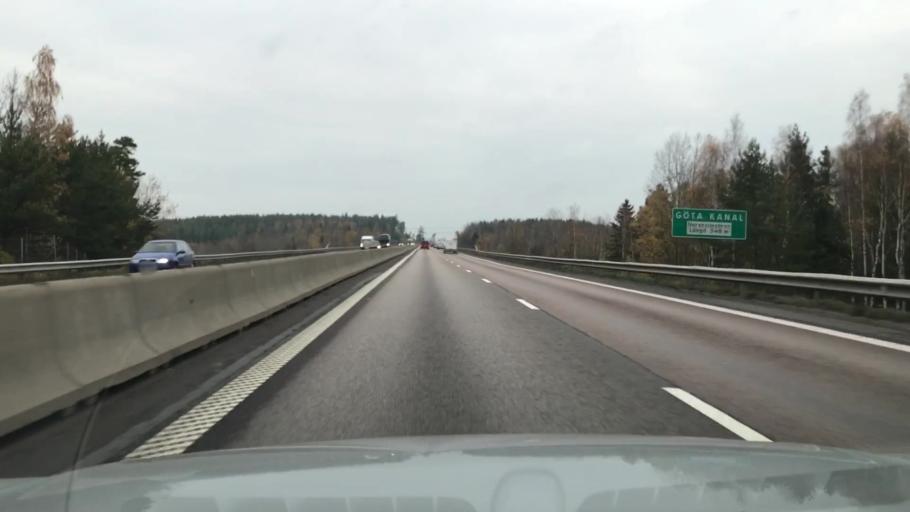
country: SE
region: OEstergoetland
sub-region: Norrkopings Kommun
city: Kimstad
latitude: 58.5081
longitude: 15.9911
